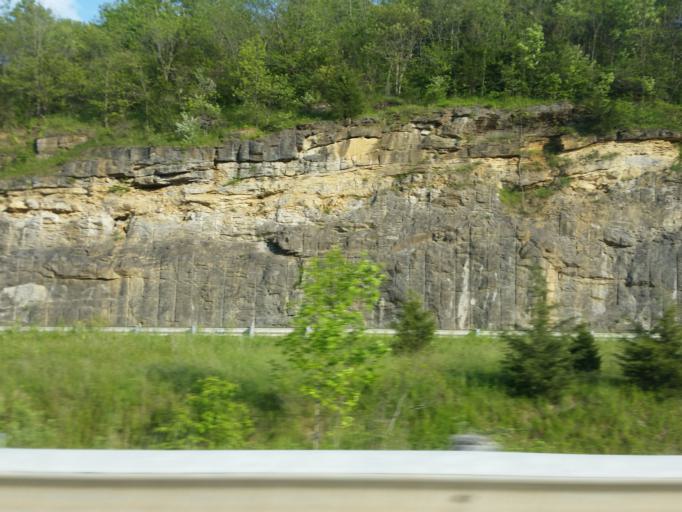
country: US
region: Virginia
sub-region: Tazewell County
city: Claypool Hill
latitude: 37.0481
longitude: -81.7794
